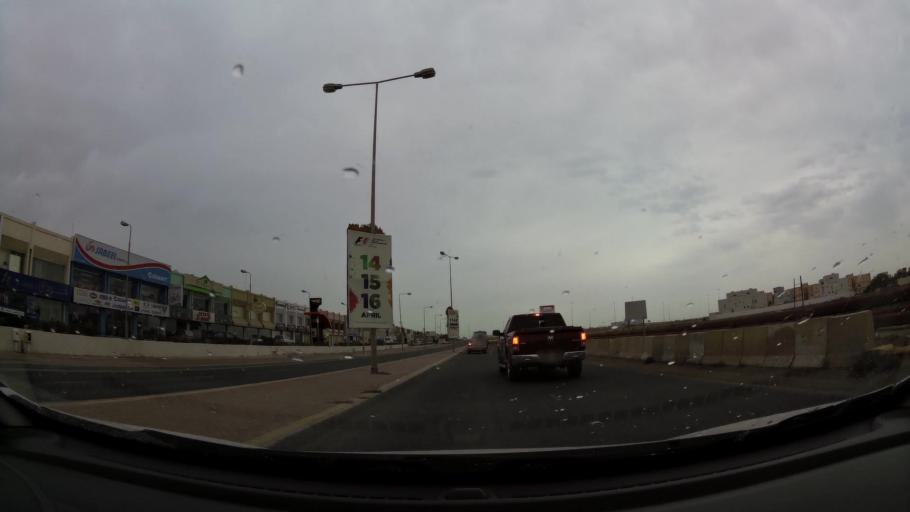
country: BH
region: Central Governorate
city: Madinat Hamad
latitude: 26.1667
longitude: 50.4683
